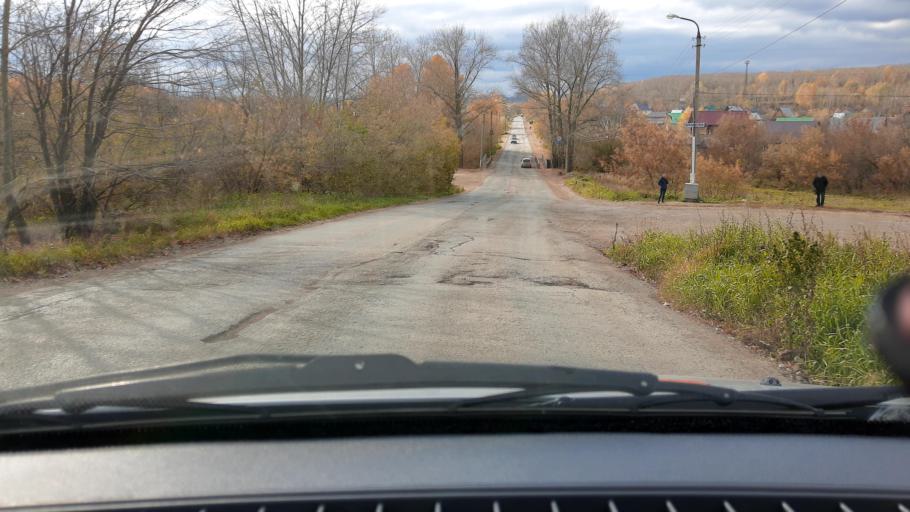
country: RU
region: Bashkortostan
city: Ufa
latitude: 54.8340
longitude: 56.1416
